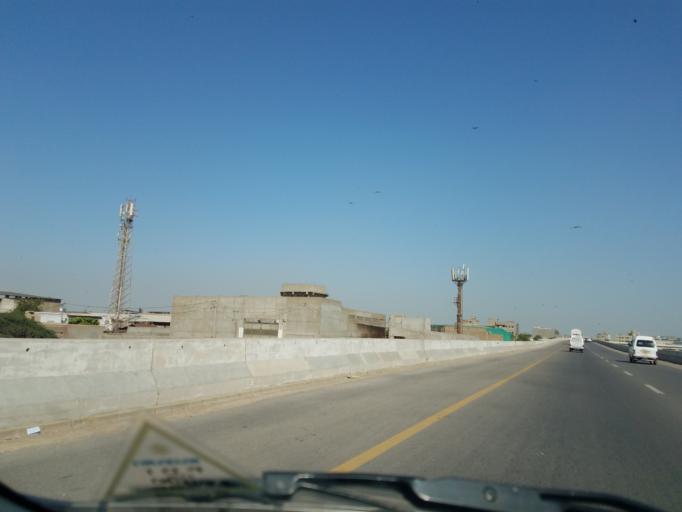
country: PK
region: Sindh
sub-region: Karachi District
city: Karachi
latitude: 24.8822
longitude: 67.0007
